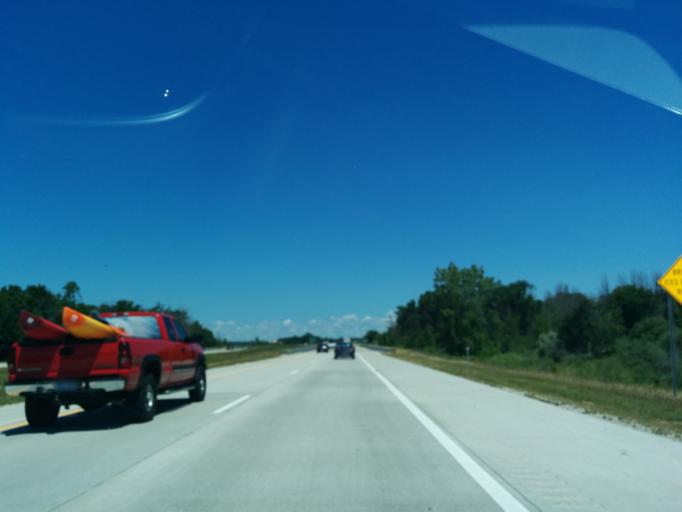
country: US
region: Michigan
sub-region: Bay County
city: Pinconning
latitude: 43.9065
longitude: -84.0199
